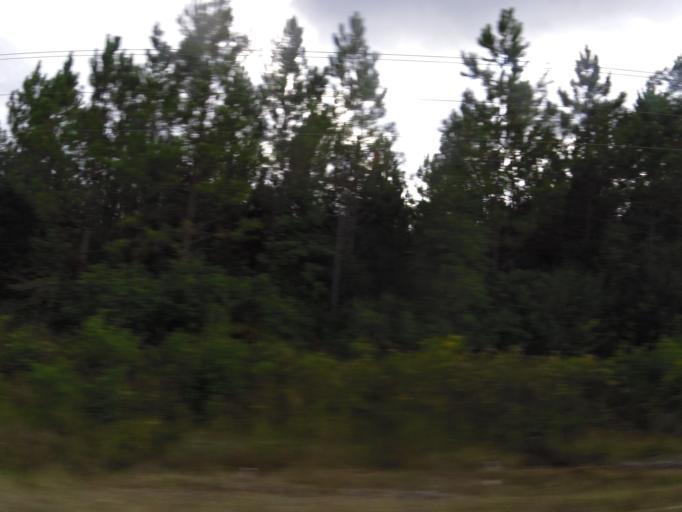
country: US
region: Florida
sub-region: Nassau County
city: Hilliard
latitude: 30.5677
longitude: -82.0441
